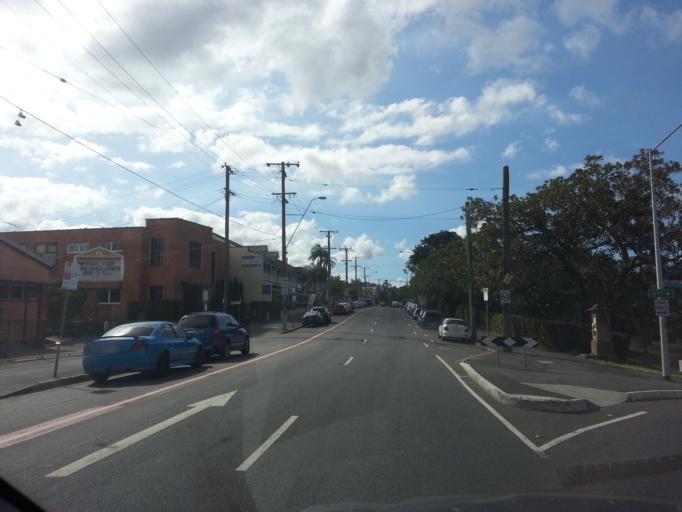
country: AU
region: Queensland
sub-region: Brisbane
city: Spring Hill
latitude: -27.4636
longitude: 153.0145
